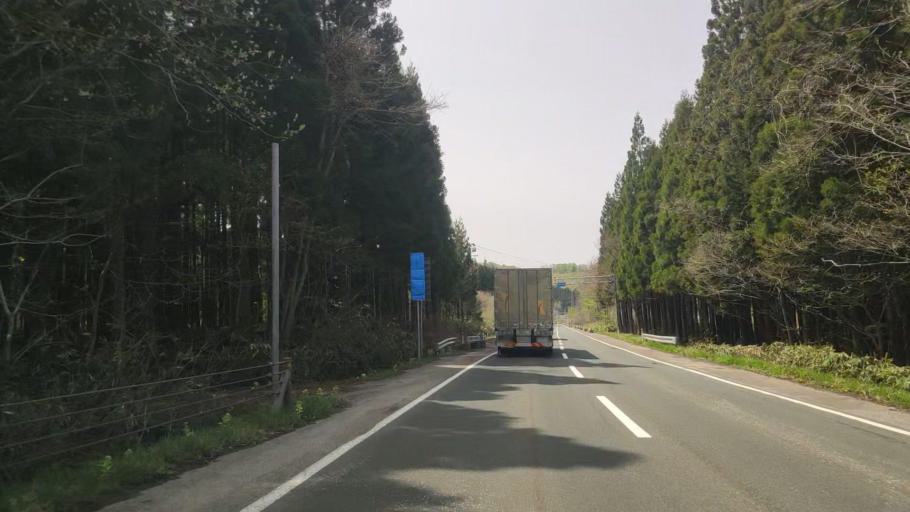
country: JP
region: Aomori
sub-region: Misawa Shi
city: Inuotose
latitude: 40.7872
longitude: 141.0806
